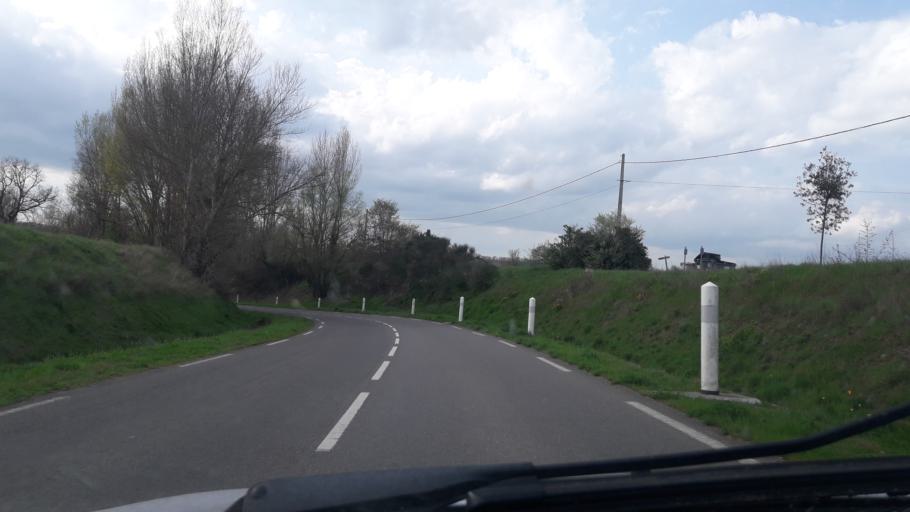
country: FR
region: Midi-Pyrenees
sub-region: Departement de la Haute-Garonne
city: Rieux-Volvestre
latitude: 43.2657
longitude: 1.2070
